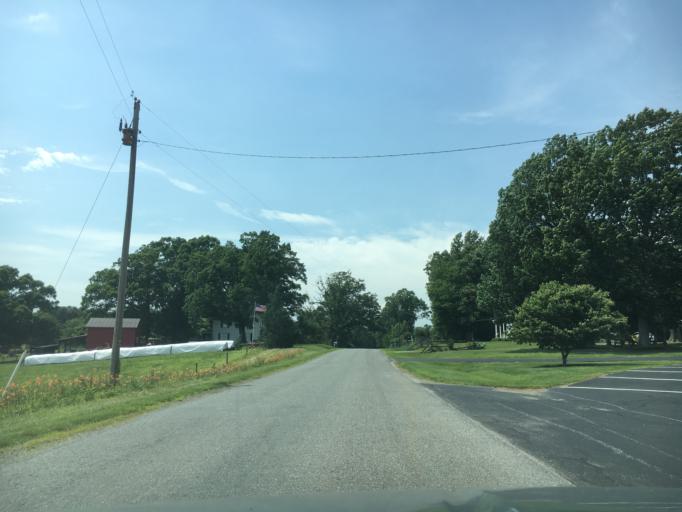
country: US
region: Virginia
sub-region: Pittsylvania County
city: Gretna
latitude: 36.9304
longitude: -79.4356
